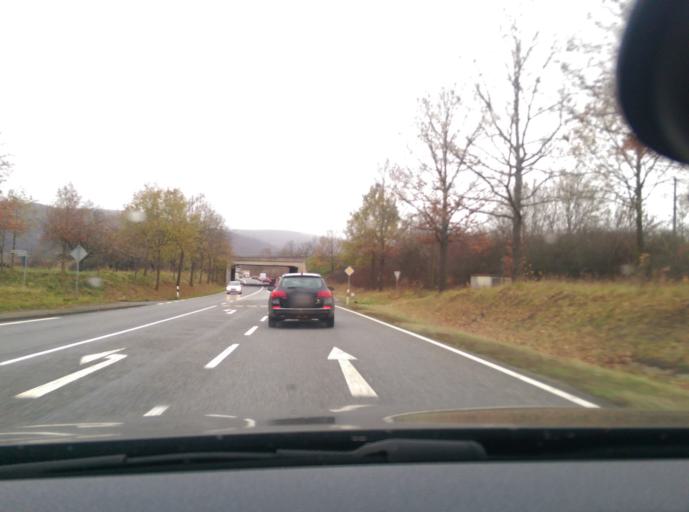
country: DE
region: Hesse
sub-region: Regierungsbezirk Kassel
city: Bad Sooden-Allendorf
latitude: 51.2589
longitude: 9.9903
